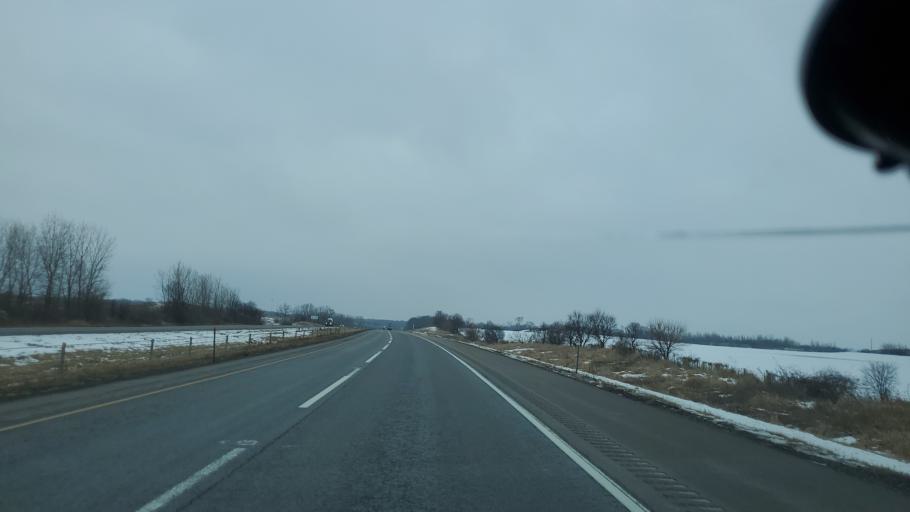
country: US
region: Illinois
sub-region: Kane County
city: Elburn
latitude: 41.8358
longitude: -88.4887
